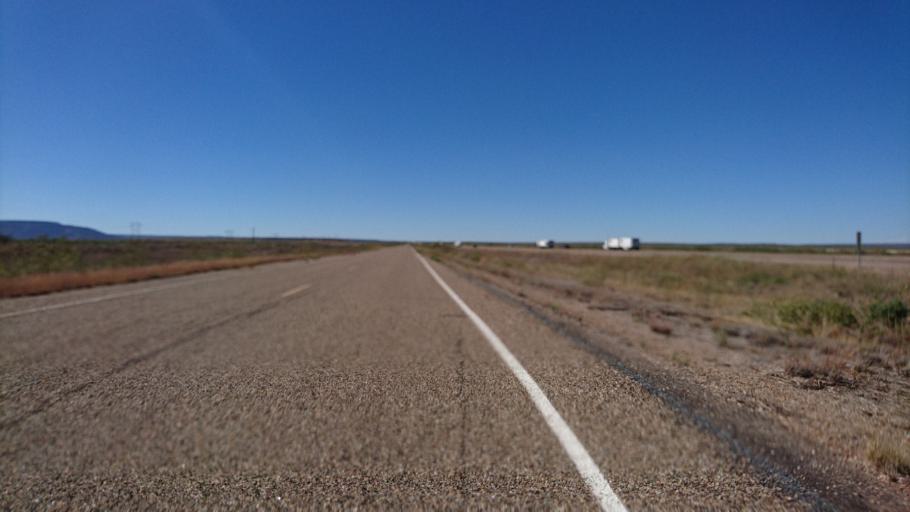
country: US
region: New Mexico
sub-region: Quay County
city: Tucumcari
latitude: 35.0910
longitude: -104.0786
